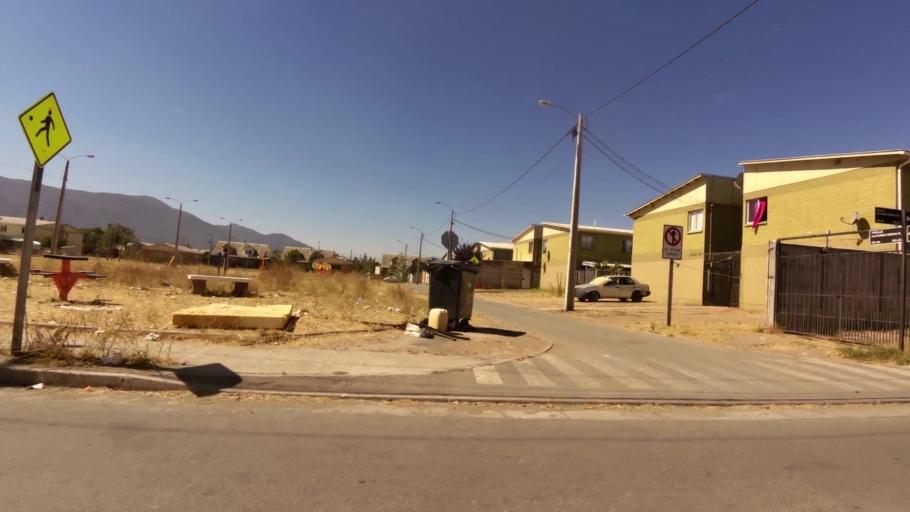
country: CL
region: O'Higgins
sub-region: Provincia de Colchagua
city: Chimbarongo
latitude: -34.5978
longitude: -71.0027
